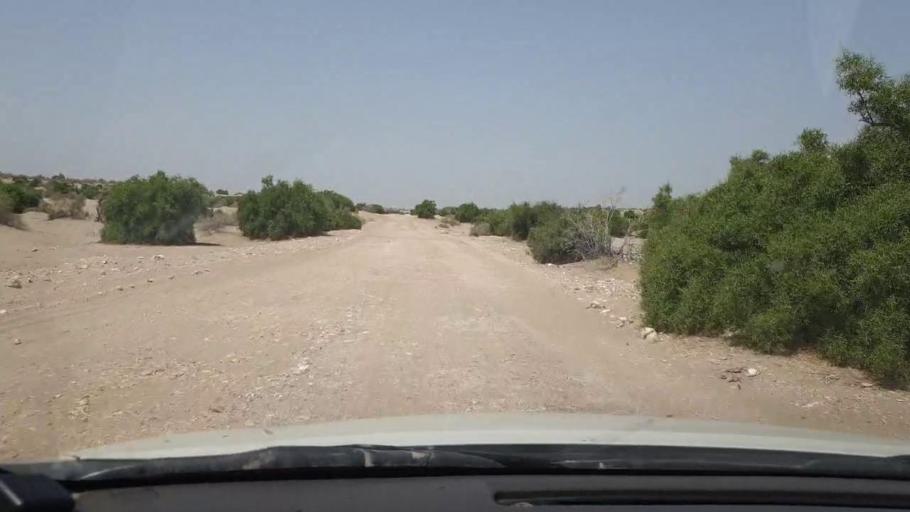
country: PK
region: Sindh
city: Rohri
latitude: 27.2891
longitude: 69.2473
